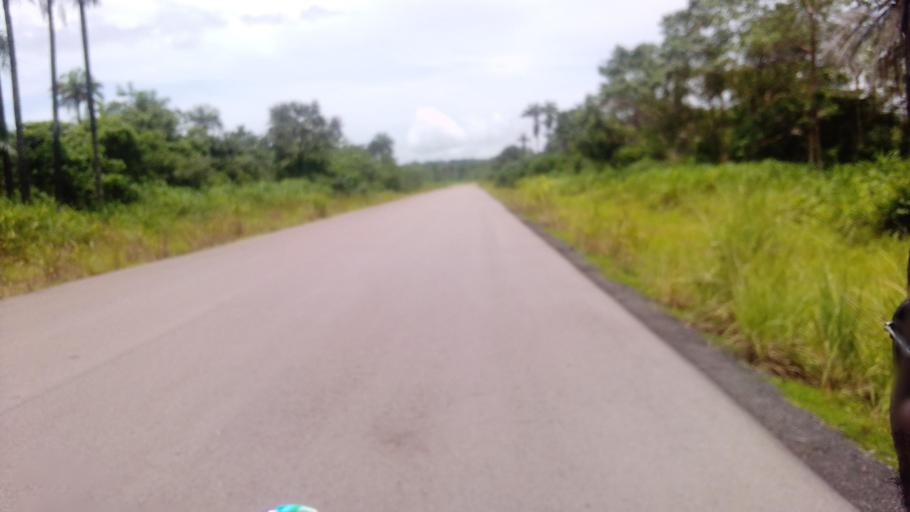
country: SL
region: Northern Province
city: Makeni
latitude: 9.0554
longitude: -12.1752
